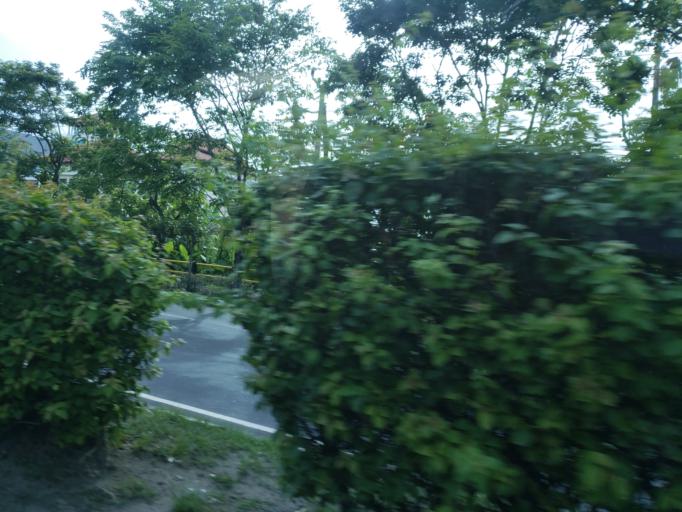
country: ID
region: Bali
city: Kuta
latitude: -8.7139
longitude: 115.1864
